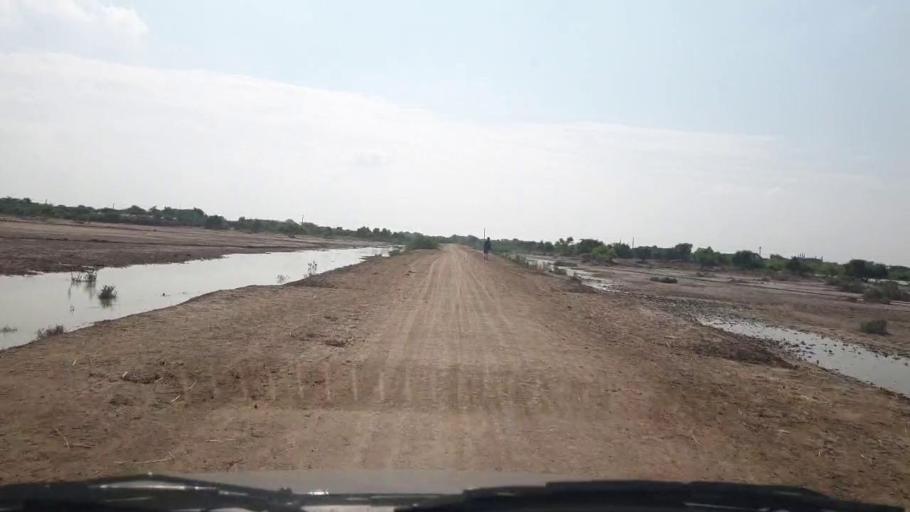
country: PK
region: Sindh
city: Badin
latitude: 24.4819
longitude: 68.6125
